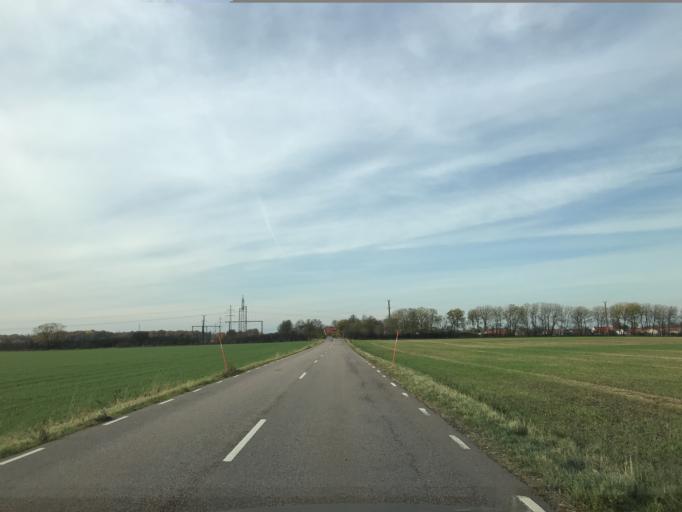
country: SE
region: Skane
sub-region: Helsingborg
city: Hyllinge
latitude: 56.0987
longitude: 12.8833
